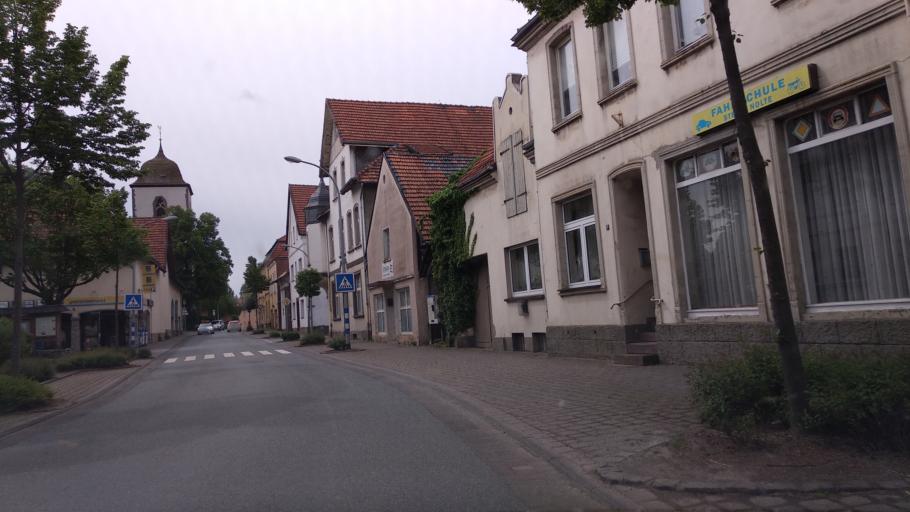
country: DE
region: North Rhine-Westphalia
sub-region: Regierungsbezirk Detmold
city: Willebadessen
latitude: 51.5985
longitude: 9.1286
